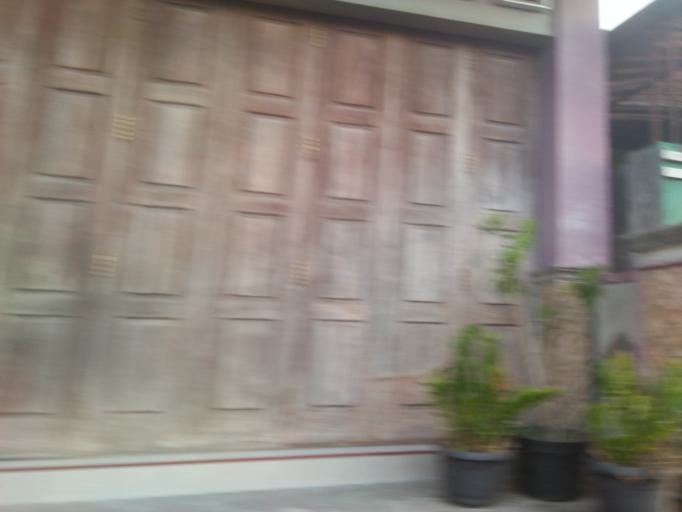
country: ID
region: Daerah Istimewa Yogyakarta
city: Sewon
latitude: -7.8562
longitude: 110.4113
